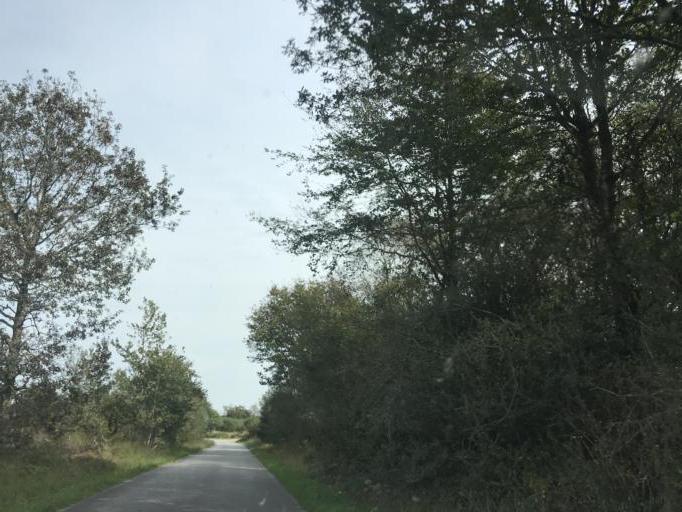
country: FR
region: Brittany
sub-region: Departement du Finistere
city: Brasparts
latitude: 48.3429
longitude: -3.8827
